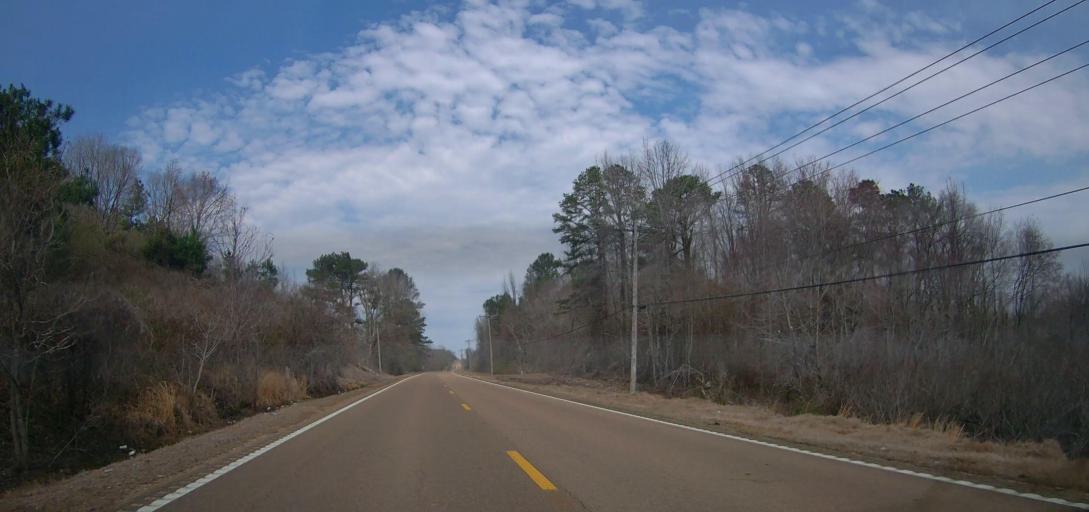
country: US
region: Mississippi
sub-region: Marshall County
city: Holly Springs
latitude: 34.7249
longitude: -89.4168
